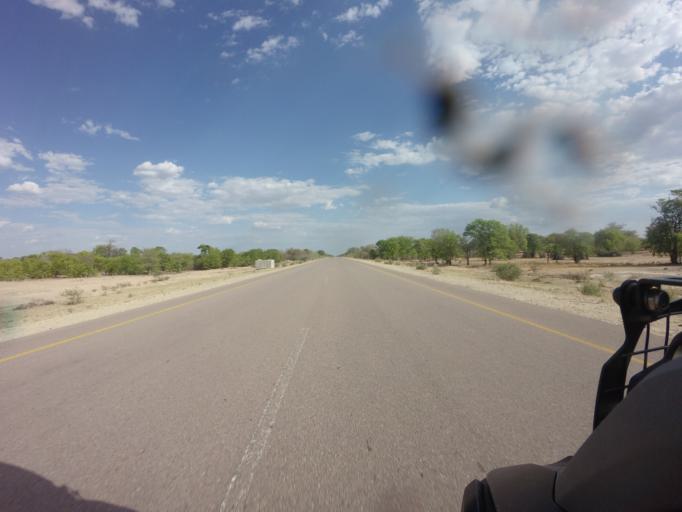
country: AO
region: Cunene
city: Ondjiva
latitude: -16.7661
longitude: 15.3948
